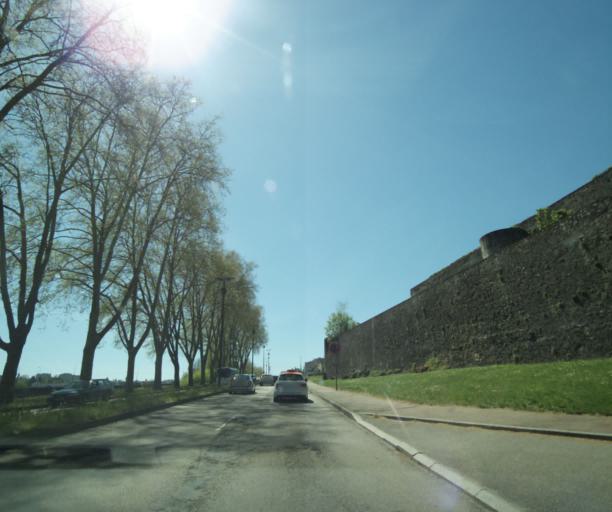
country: FR
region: Limousin
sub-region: Departement de la Haute-Vienne
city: Limoges
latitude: 45.8278
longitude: 1.2688
